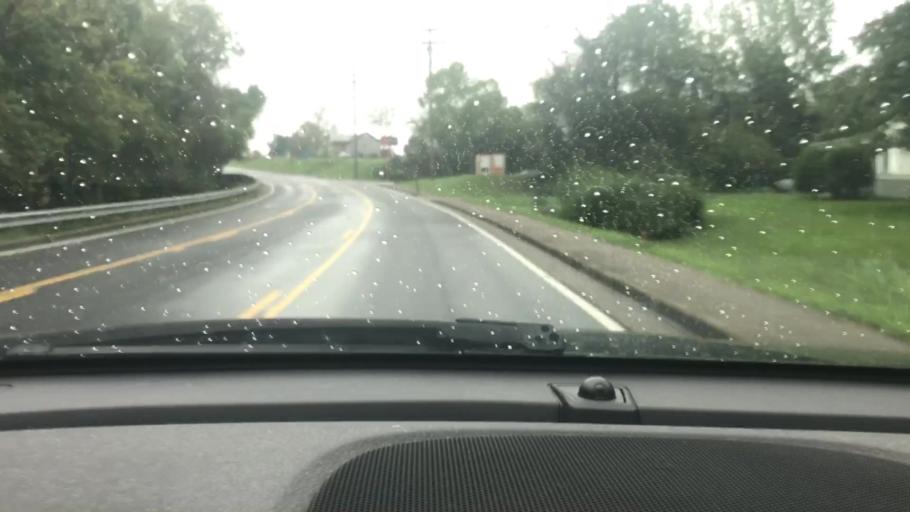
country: US
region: Tennessee
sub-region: Cheatham County
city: Kingston Springs
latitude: 36.0881
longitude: -87.1057
